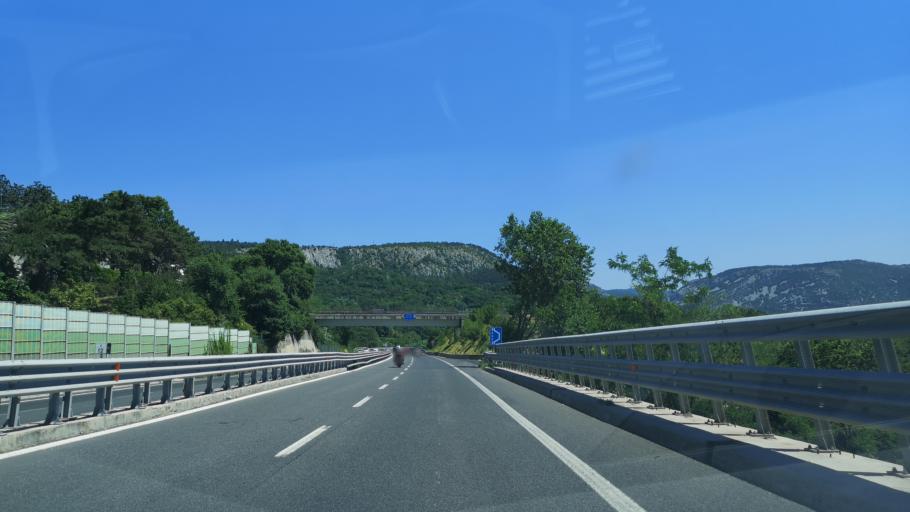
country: IT
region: Friuli Venezia Giulia
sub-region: Provincia di Trieste
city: Domio
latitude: 45.6301
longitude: 13.8237
